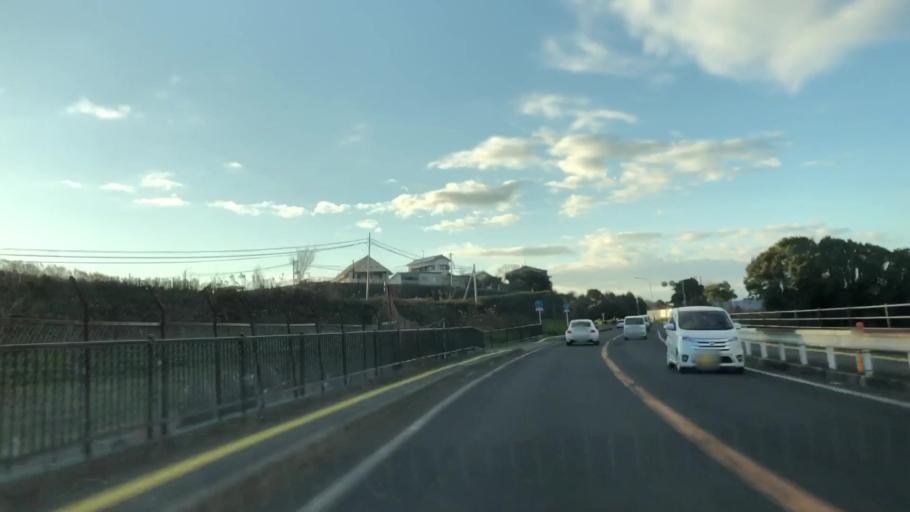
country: JP
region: Oita
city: Bungo-Takada-shi
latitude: 33.5353
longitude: 131.3132
